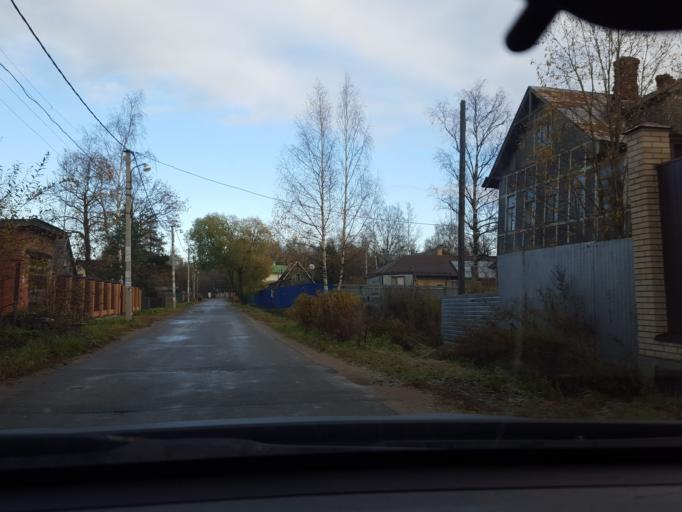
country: RU
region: St.-Petersburg
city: Shuvalovo
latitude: 60.0412
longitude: 30.2958
